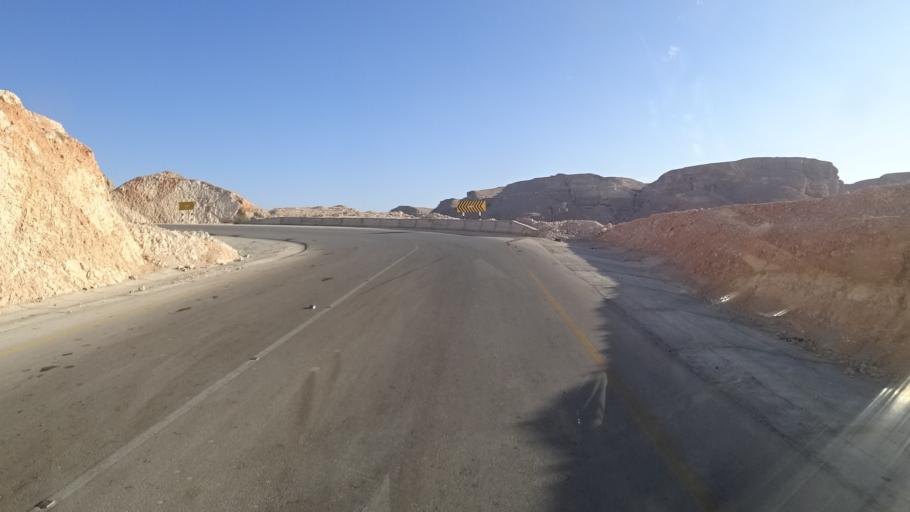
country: YE
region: Al Mahrah
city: Hawf
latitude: 17.0934
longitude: 53.0587
